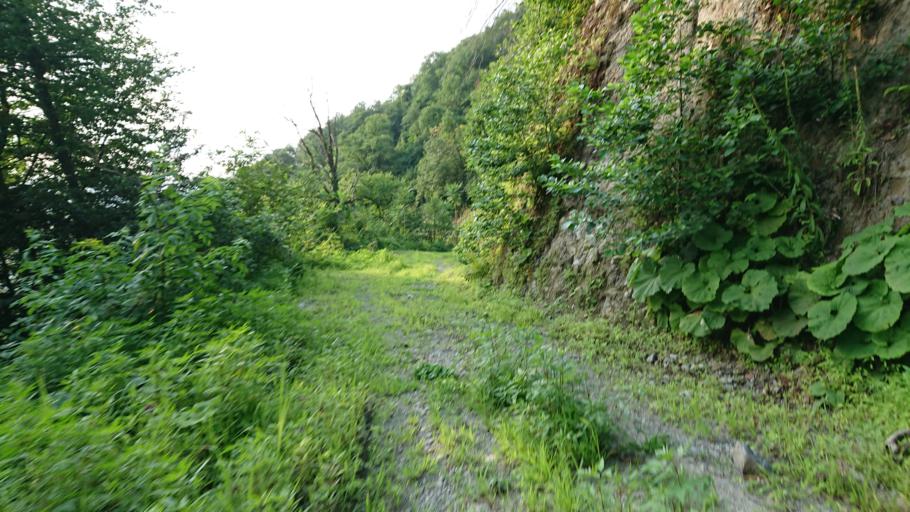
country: TR
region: Rize
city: Rize
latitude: 40.9893
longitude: 40.5038
